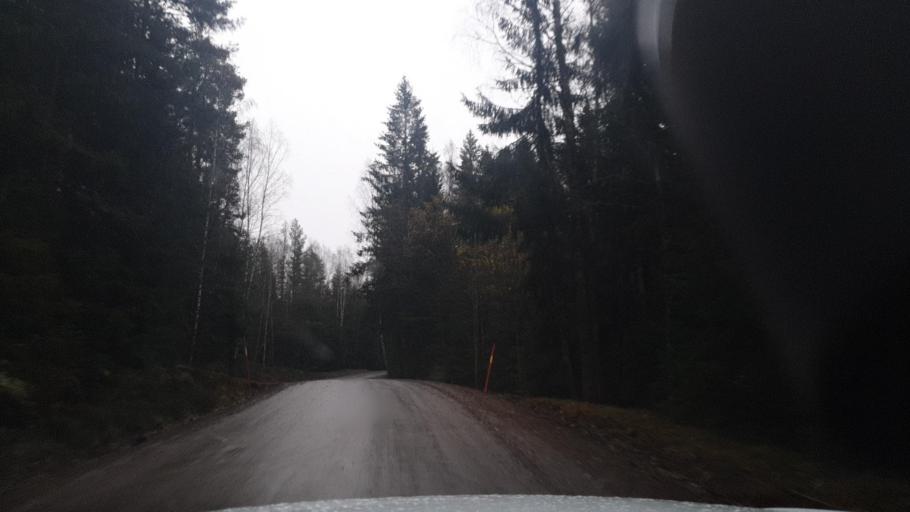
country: SE
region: Vaermland
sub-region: Eda Kommun
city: Charlottenberg
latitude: 59.7308
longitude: 12.1137
